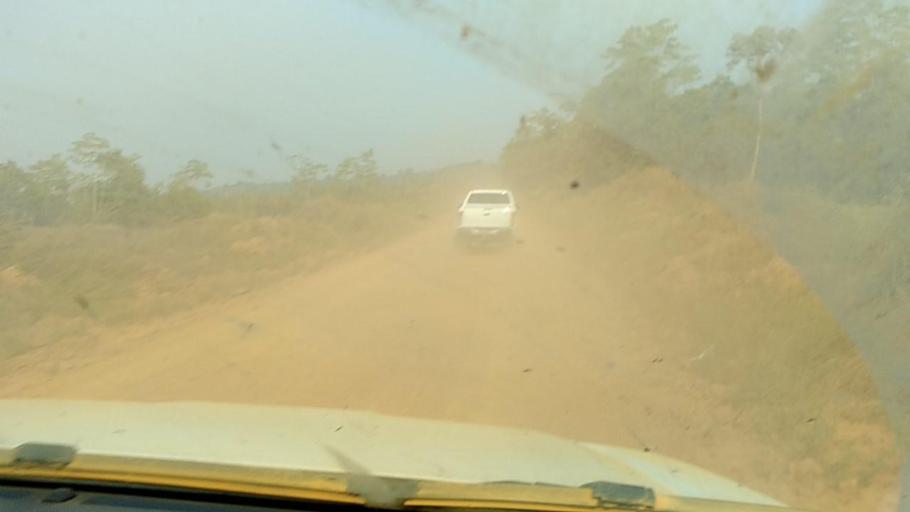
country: BR
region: Rondonia
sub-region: Porto Velho
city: Porto Velho
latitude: -8.7607
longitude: -64.0649
